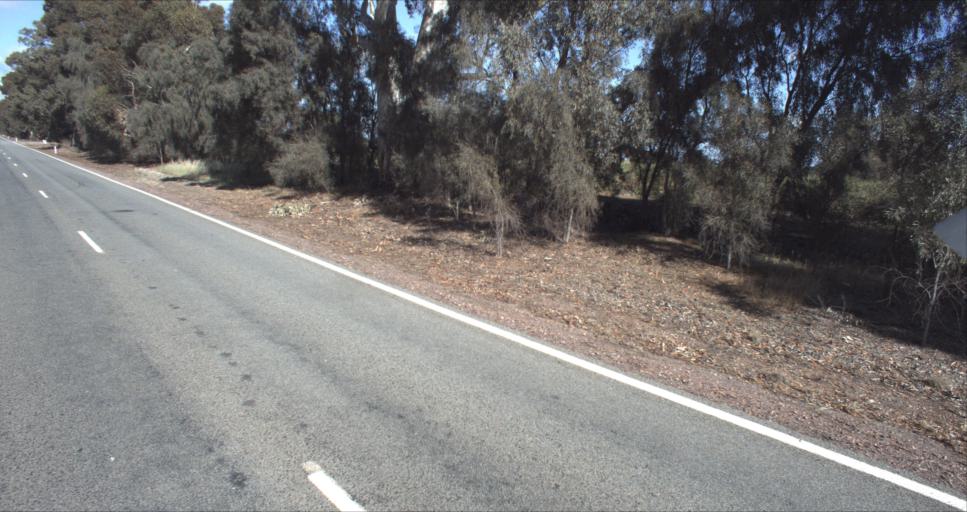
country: AU
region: New South Wales
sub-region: Leeton
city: Leeton
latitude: -34.5444
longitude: 146.3304
